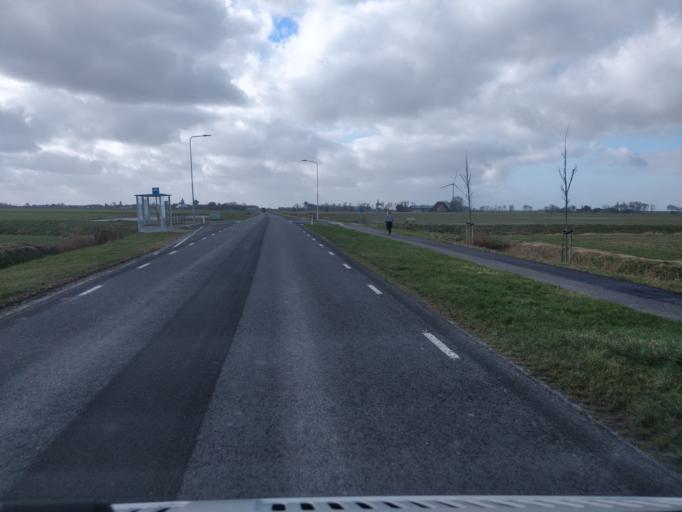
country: NL
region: Friesland
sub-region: Gemeente Franekeradeel
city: Sexbierum
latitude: 53.2311
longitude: 5.5039
